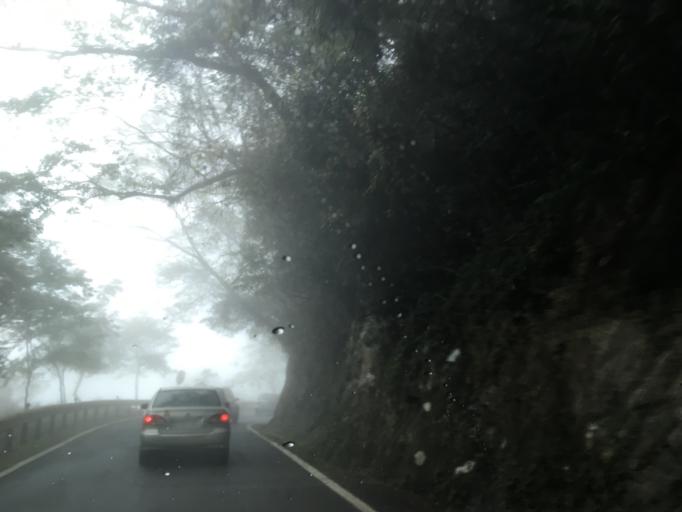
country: TW
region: Taiwan
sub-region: Hualien
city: Hualian
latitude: 24.1861
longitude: 121.4165
